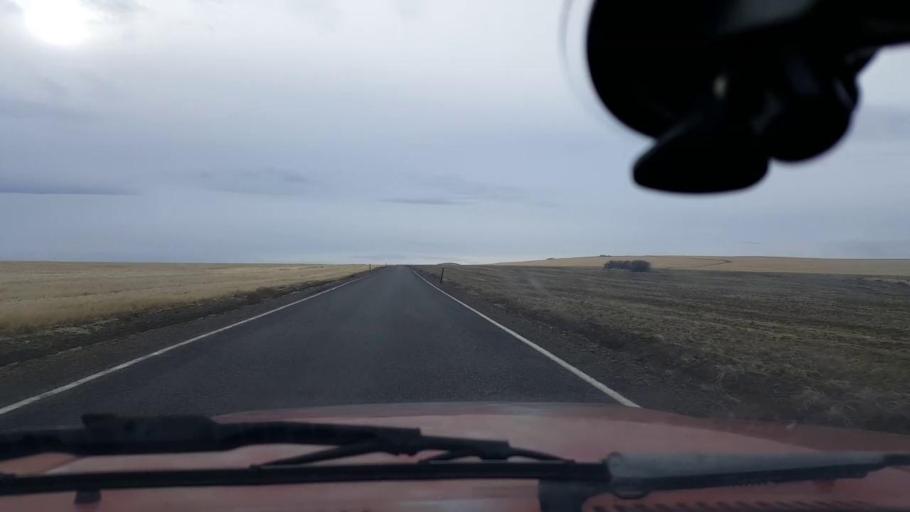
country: US
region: Washington
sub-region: Asotin County
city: Clarkston Heights-Vineland
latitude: 46.3497
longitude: -117.2342
